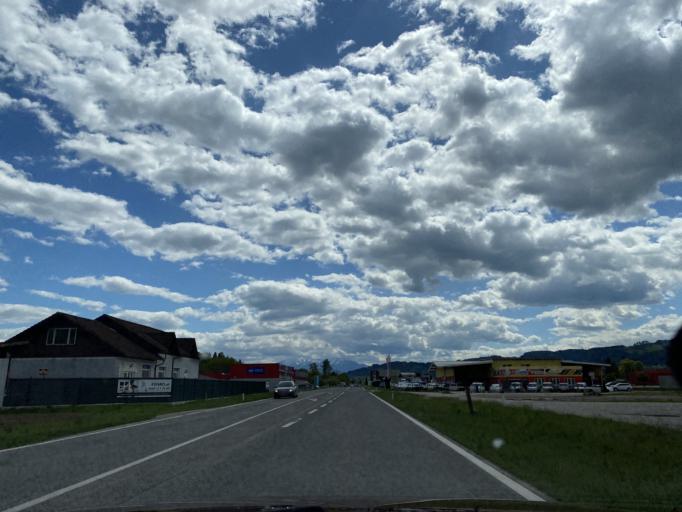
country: AT
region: Carinthia
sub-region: Politischer Bezirk Wolfsberg
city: Wolfsberg
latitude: 46.8056
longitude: 14.8301
